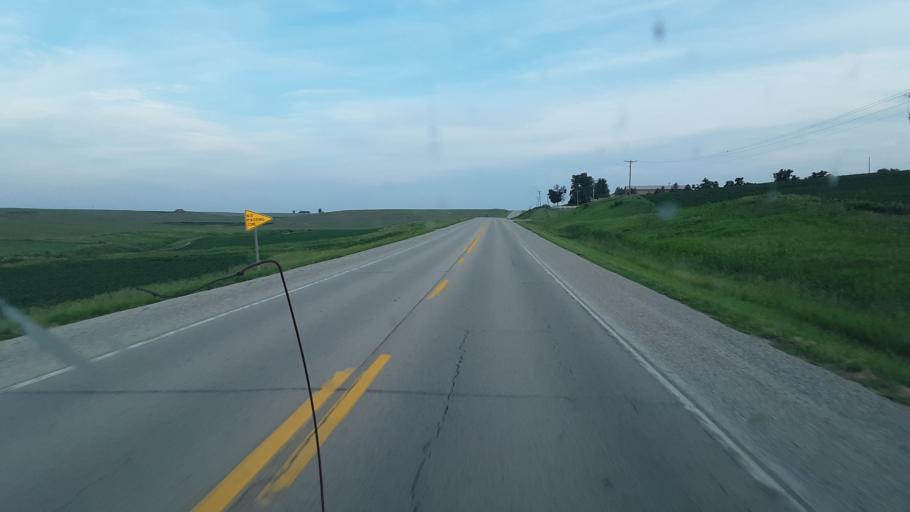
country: US
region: Iowa
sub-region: Benton County
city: Belle Plaine
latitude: 41.7740
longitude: -92.2791
